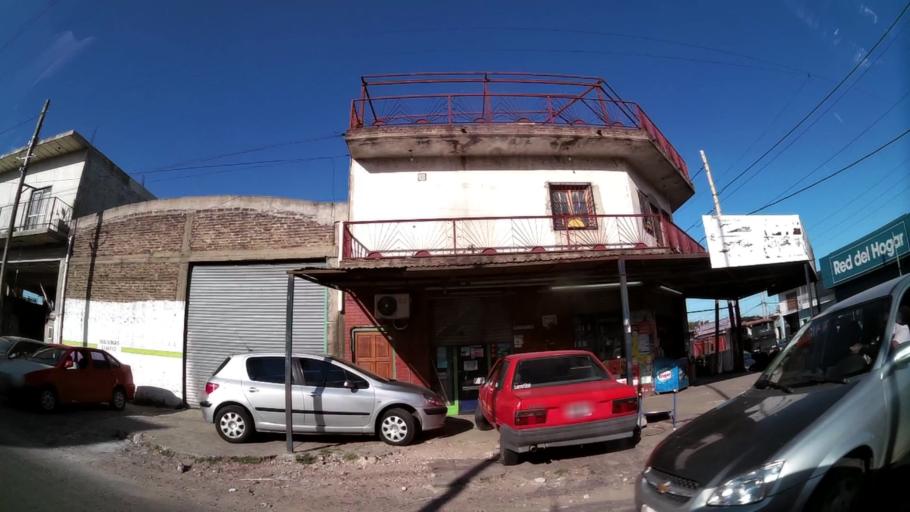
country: AR
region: Buenos Aires
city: Hurlingham
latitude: -34.5062
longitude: -58.7222
